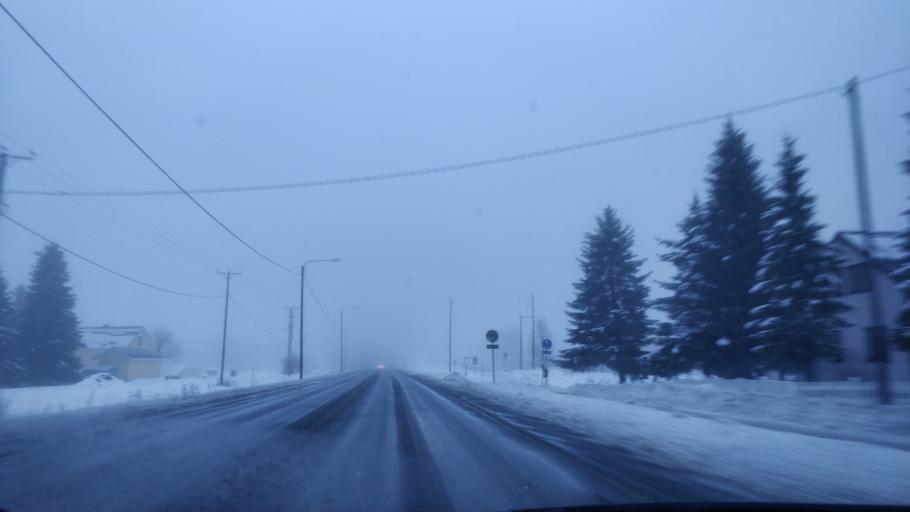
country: FI
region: Lapland
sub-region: Kemi-Tornio
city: Tervola
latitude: 66.1390
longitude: 24.9394
